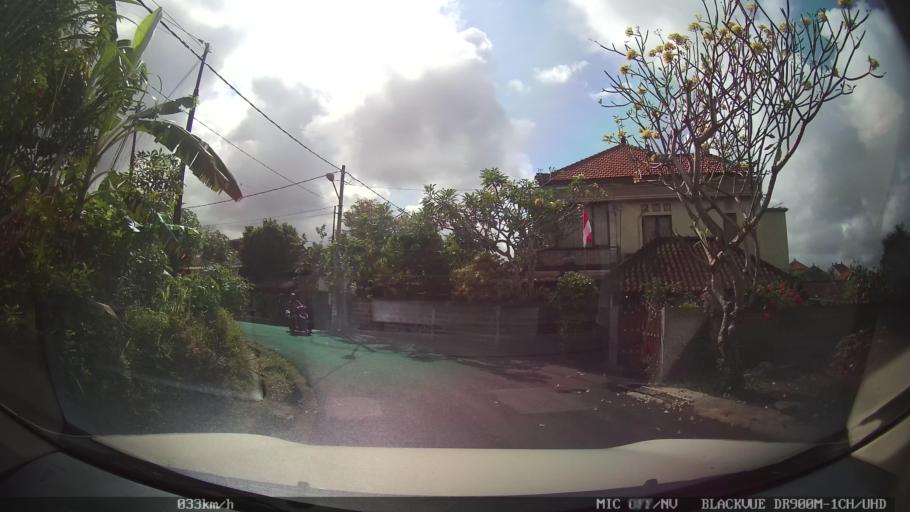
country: ID
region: Bali
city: Banjar Batur
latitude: -8.6072
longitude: 115.2045
